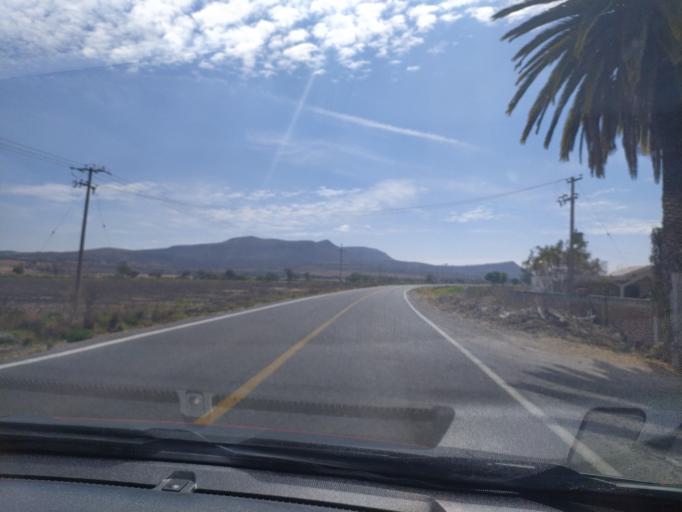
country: MX
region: Guanajuato
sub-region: San Francisco del Rincon
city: San Ignacio de Hidalgo
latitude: 20.8482
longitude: -101.8500
